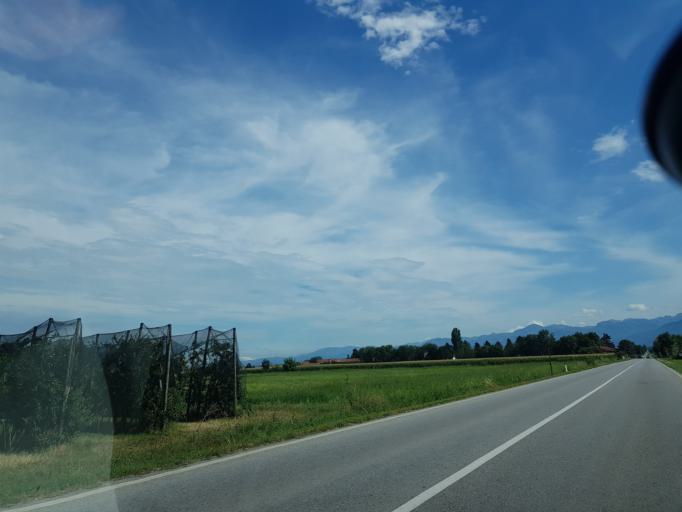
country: IT
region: Piedmont
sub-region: Provincia di Cuneo
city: Roata Rossi
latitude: 44.4668
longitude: 7.5143
